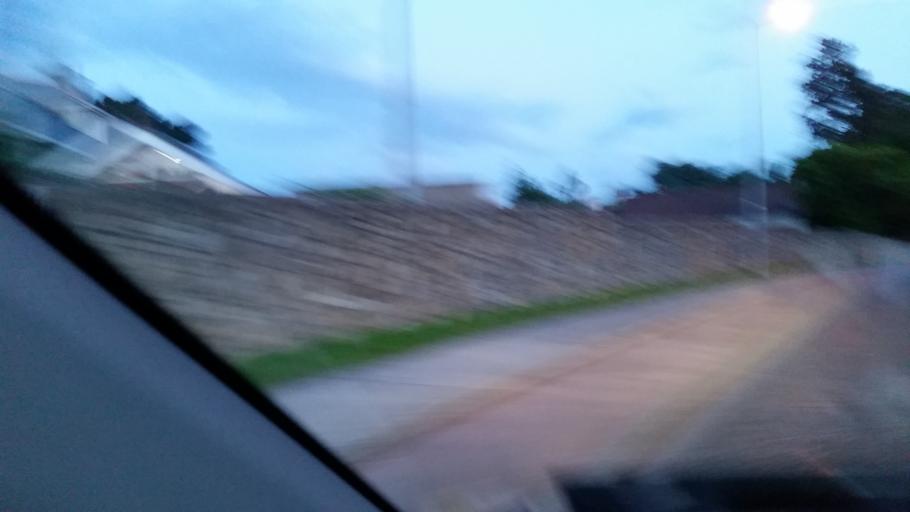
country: IE
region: Leinster
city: Foxrock
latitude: 53.2579
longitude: -6.1703
